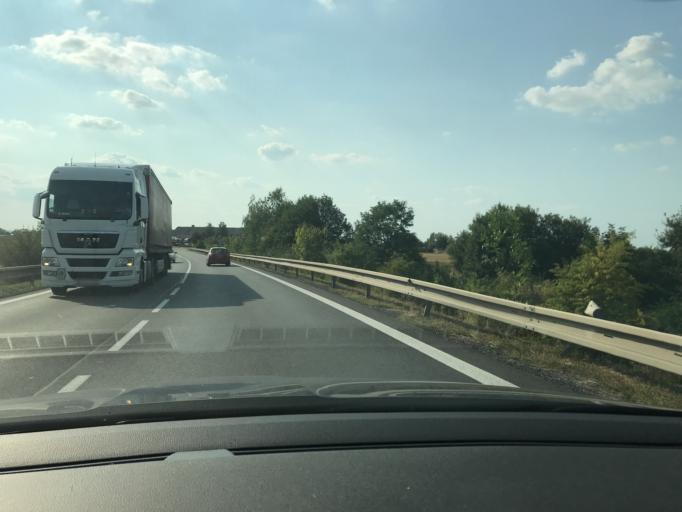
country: CZ
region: Central Bohemia
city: Velvary
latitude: 50.2720
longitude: 14.2309
